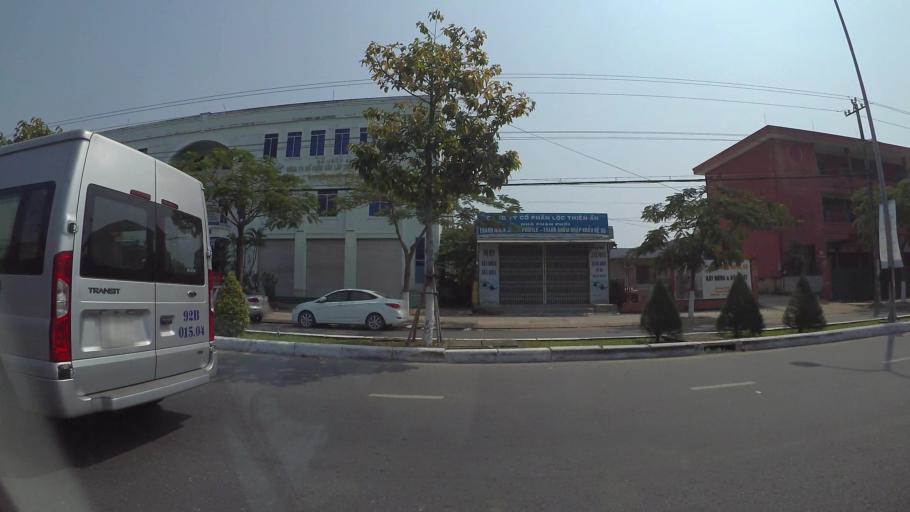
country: VN
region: Da Nang
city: Son Tra
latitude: 16.0503
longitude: 108.2379
